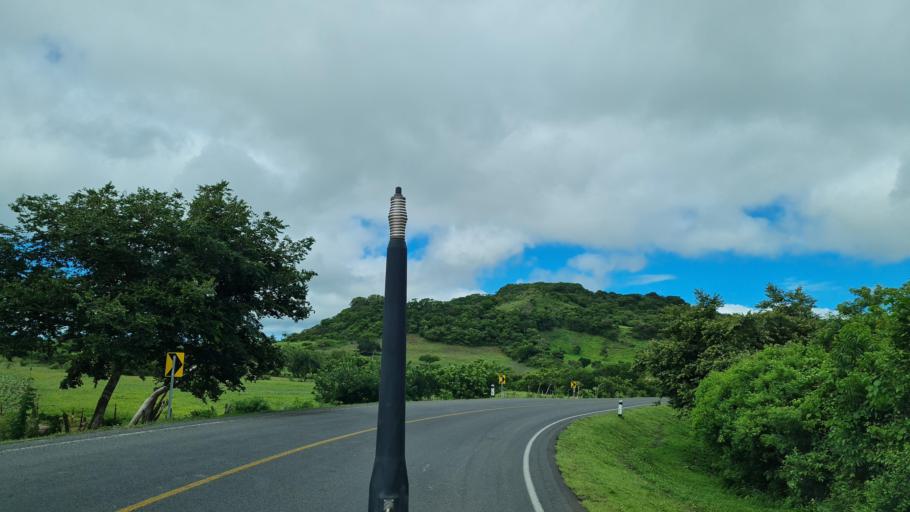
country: NI
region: Matagalpa
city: Terrabona
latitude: 12.5837
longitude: -85.9732
